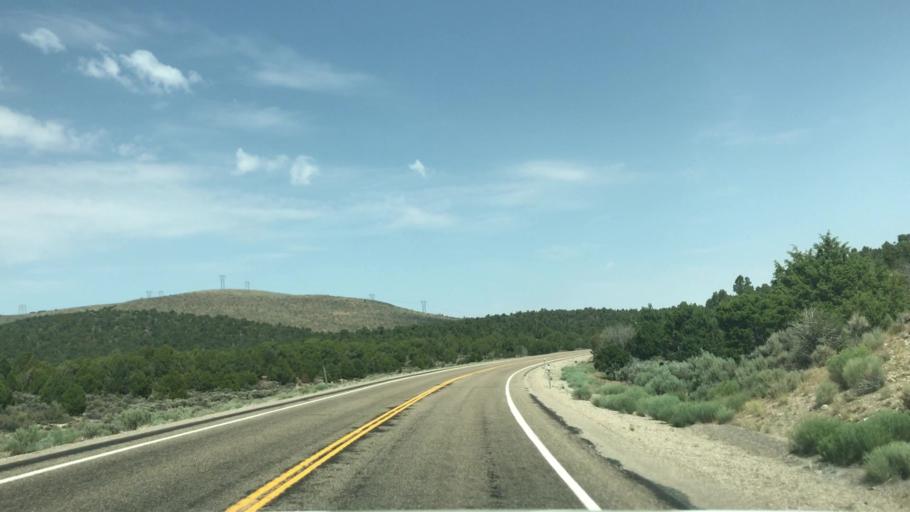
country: US
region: Nevada
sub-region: White Pine County
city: Ely
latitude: 39.3932
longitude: -115.0825
